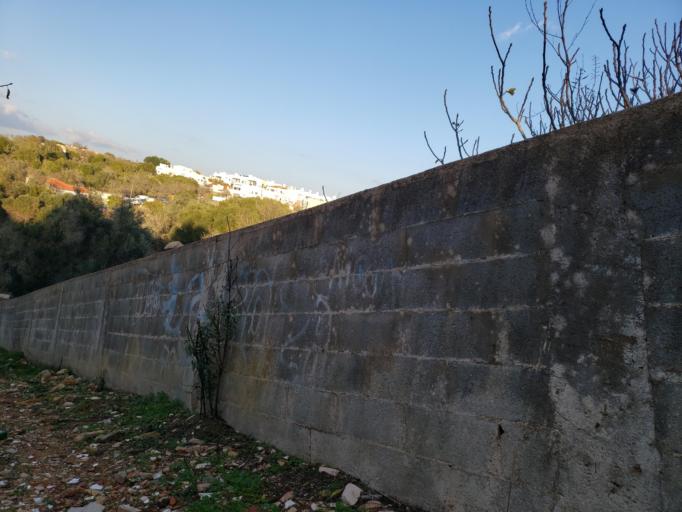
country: PT
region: Faro
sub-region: Portimao
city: Alvor
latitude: 37.1319
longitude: -8.5947
